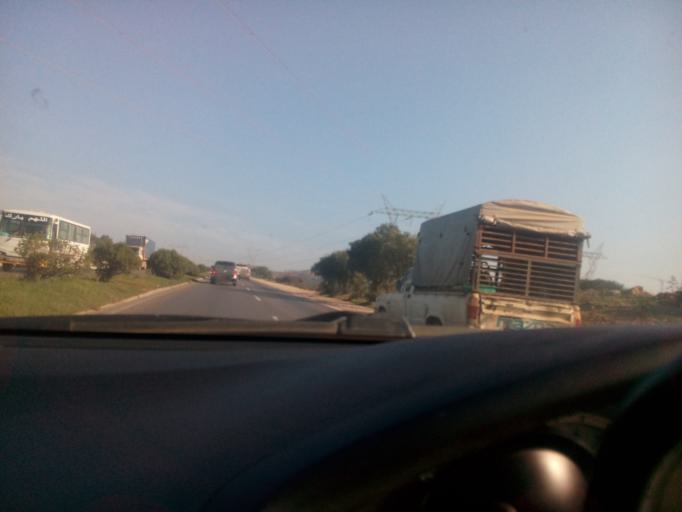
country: DZ
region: Oran
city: Oran
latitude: 35.6416
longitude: -0.7095
